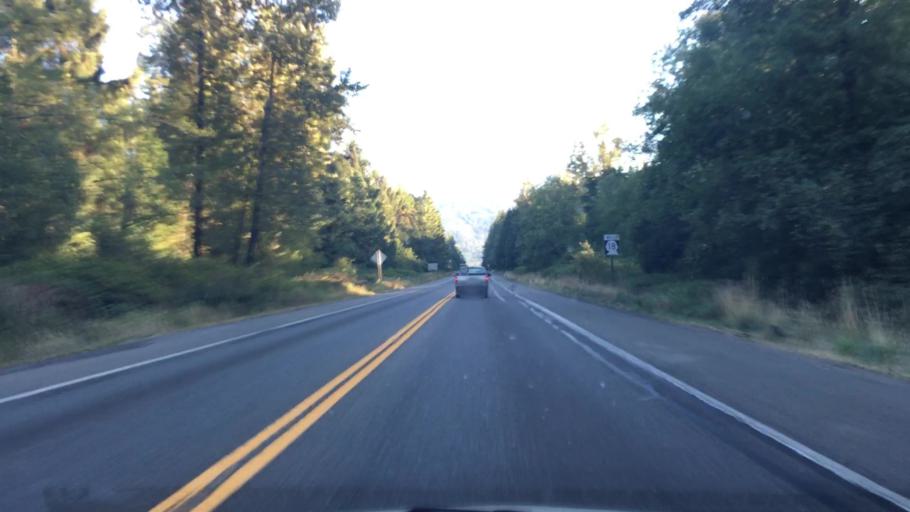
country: US
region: Washington
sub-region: King County
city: Fall City
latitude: 47.5028
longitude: -121.8851
